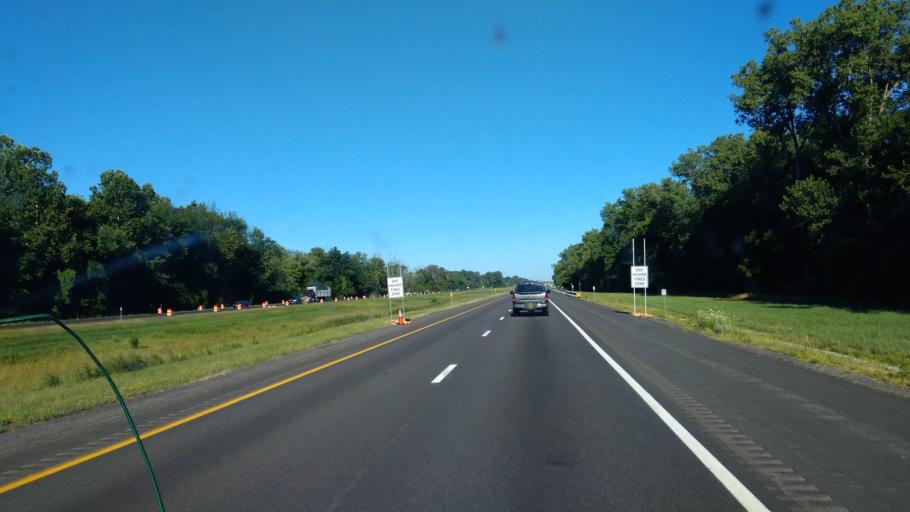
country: US
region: New York
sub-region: Ontario County
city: Clifton Springs
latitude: 42.9734
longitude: -77.1432
